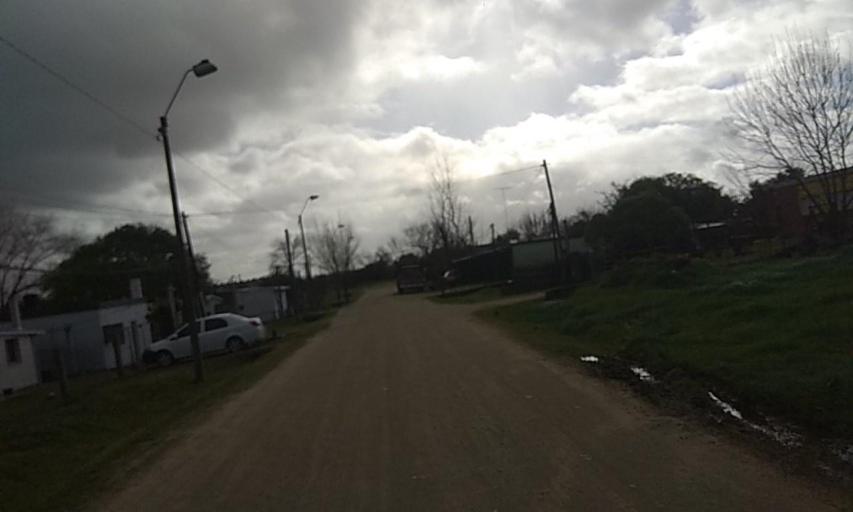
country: UY
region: Florida
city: Florida
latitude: -34.0911
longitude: -56.1994
